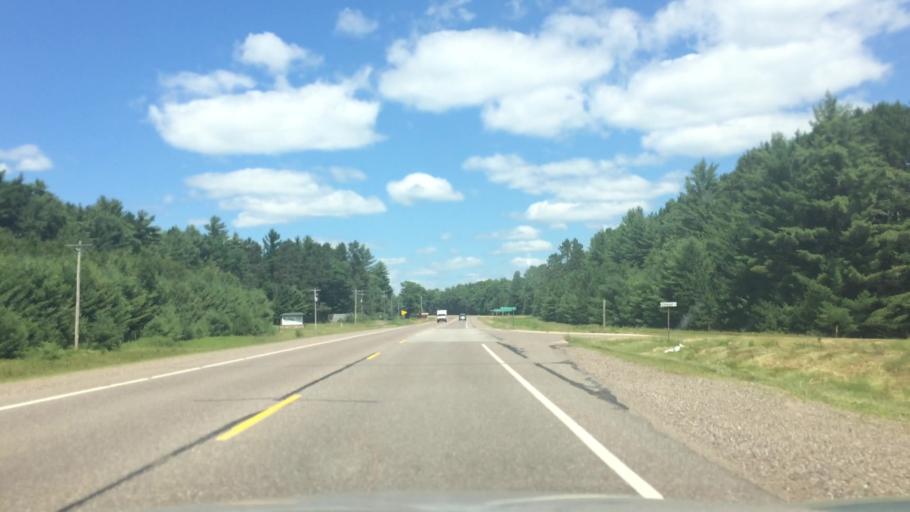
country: US
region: Wisconsin
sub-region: Vilas County
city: Lac du Flambeau
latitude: 45.9368
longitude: -89.6966
